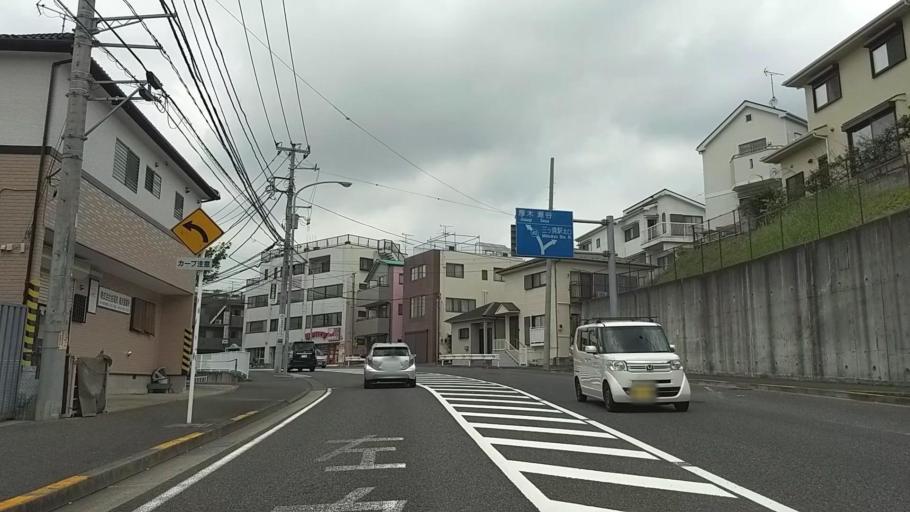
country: JP
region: Kanagawa
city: Minami-rinkan
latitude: 35.4666
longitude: 139.5074
